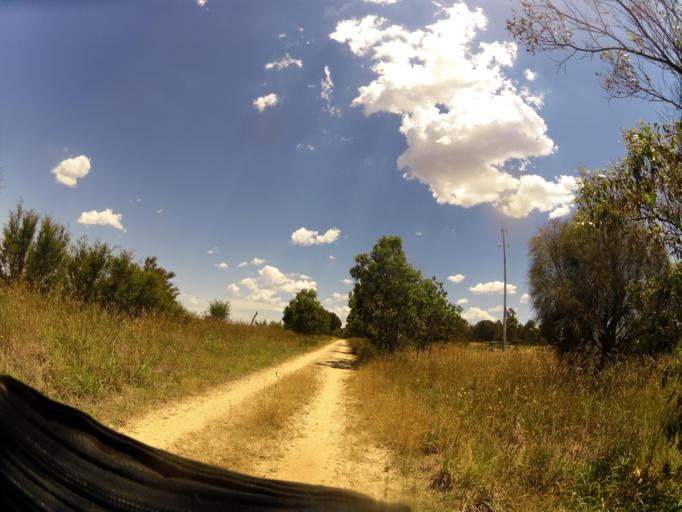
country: AU
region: Victoria
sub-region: Wellington
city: Heyfield
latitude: -37.9787
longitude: 146.8509
